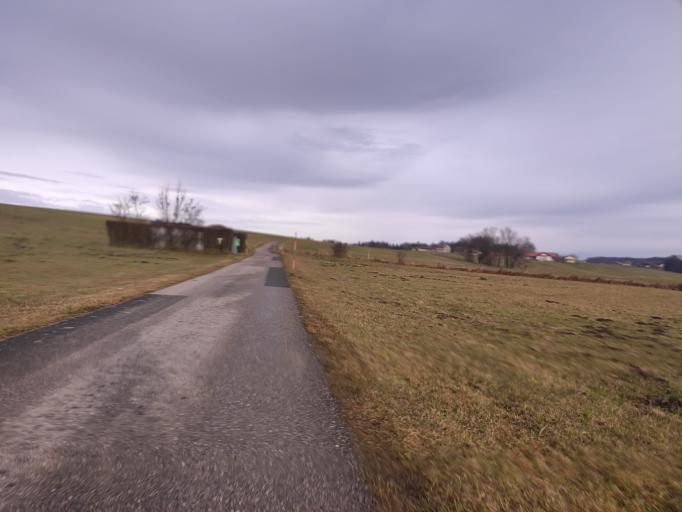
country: AT
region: Salzburg
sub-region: Politischer Bezirk Salzburg-Umgebung
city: Elixhausen
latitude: 47.8694
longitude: 13.0482
